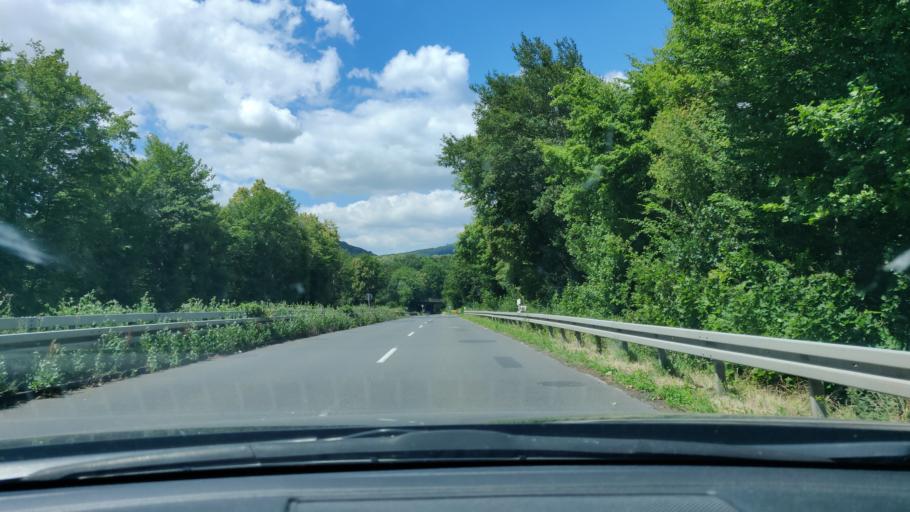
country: DE
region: Hesse
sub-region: Regierungsbezirk Kassel
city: Baunatal
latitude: 51.2635
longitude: 9.4338
